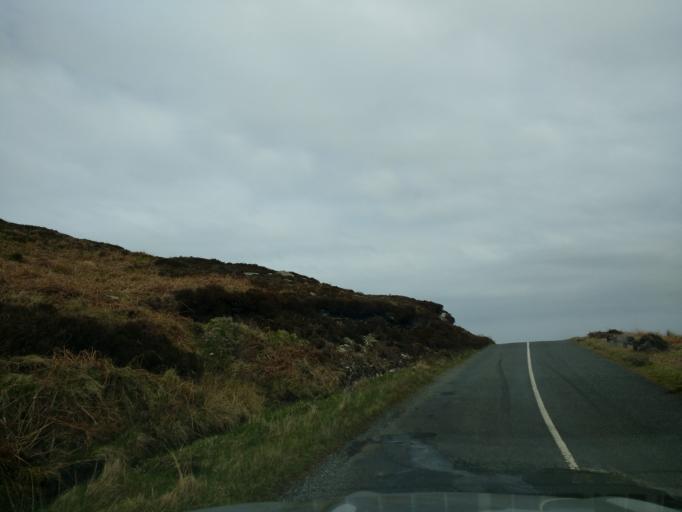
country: IE
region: Ulster
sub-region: County Donegal
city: Buncrana
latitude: 55.1824
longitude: -7.5866
